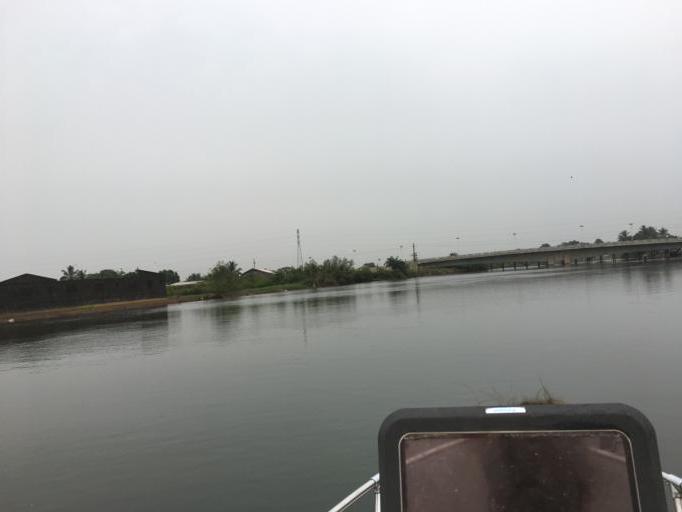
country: LR
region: Montserrado
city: Monrovia
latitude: 6.3751
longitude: -10.7802
